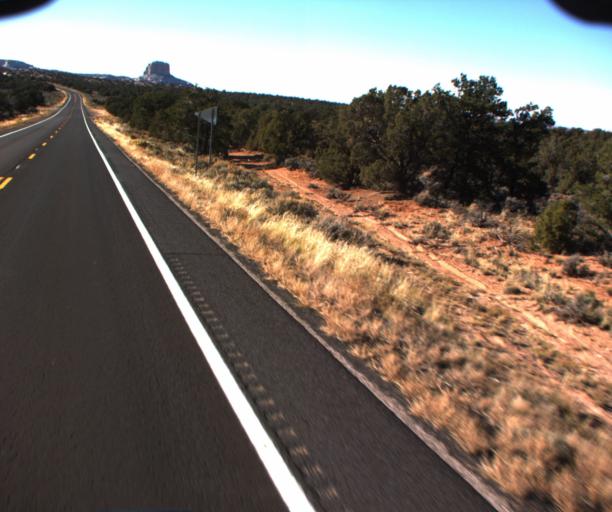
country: US
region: Arizona
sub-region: Coconino County
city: Kaibito
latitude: 36.5894
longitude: -110.8793
